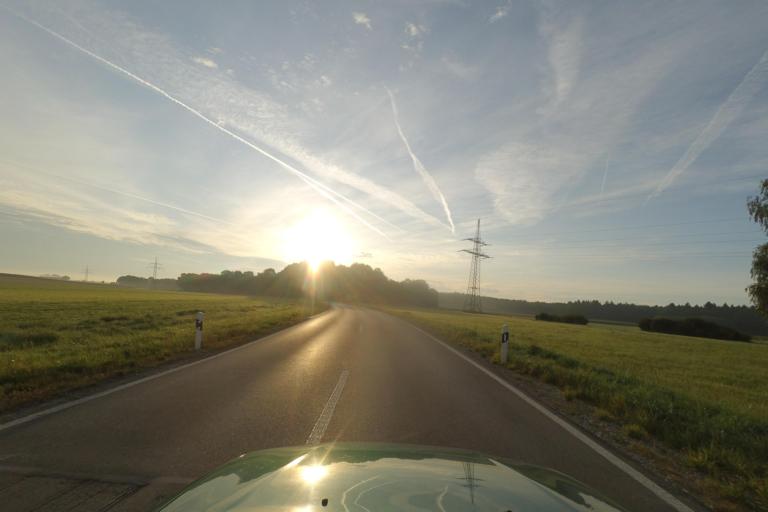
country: DE
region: Bavaria
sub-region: Upper Bavaria
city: Moorenweis
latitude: 48.1504
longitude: 11.1063
